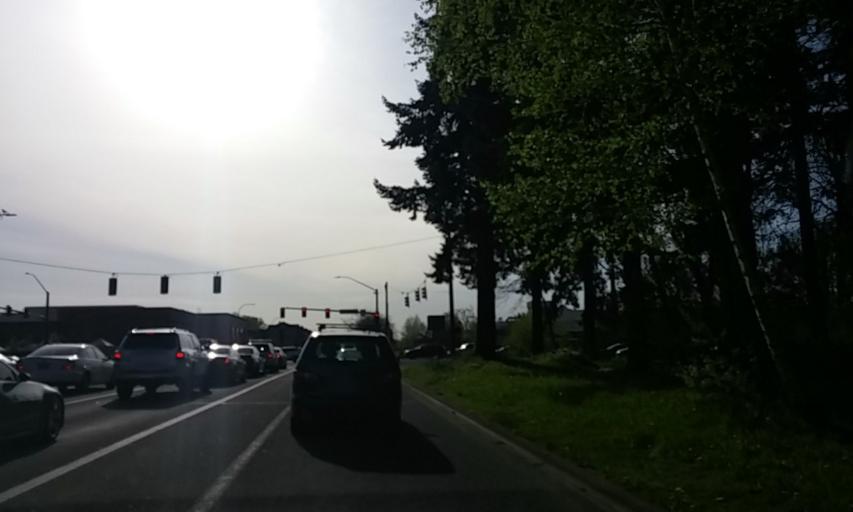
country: US
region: Oregon
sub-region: Washington County
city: Cedar Mill
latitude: 45.5040
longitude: -122.8276
